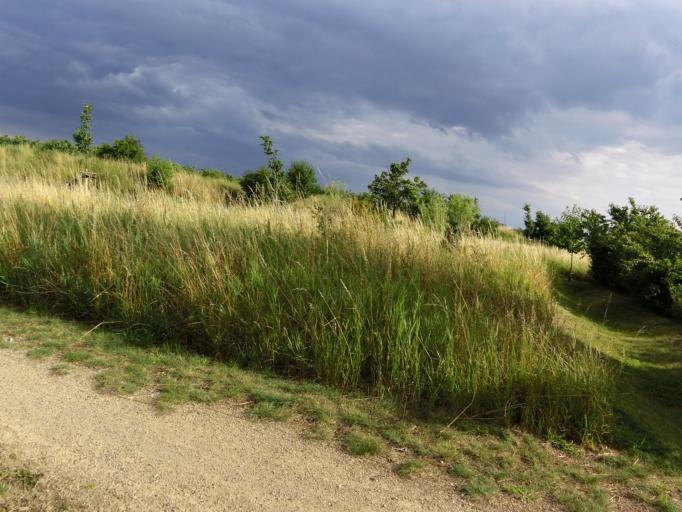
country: DE
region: Saxony
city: Zwenkau
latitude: 51.2667
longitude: 12.2963
